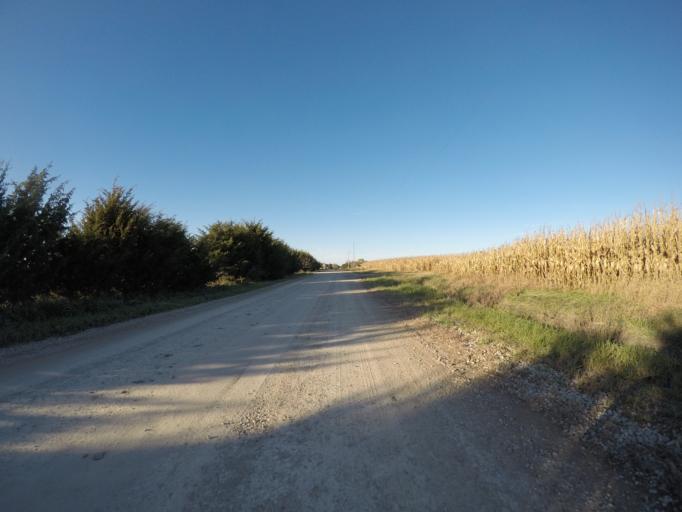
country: US
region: Kansas
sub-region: Riley County
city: Ogden
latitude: 39.2662
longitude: -96.7193
